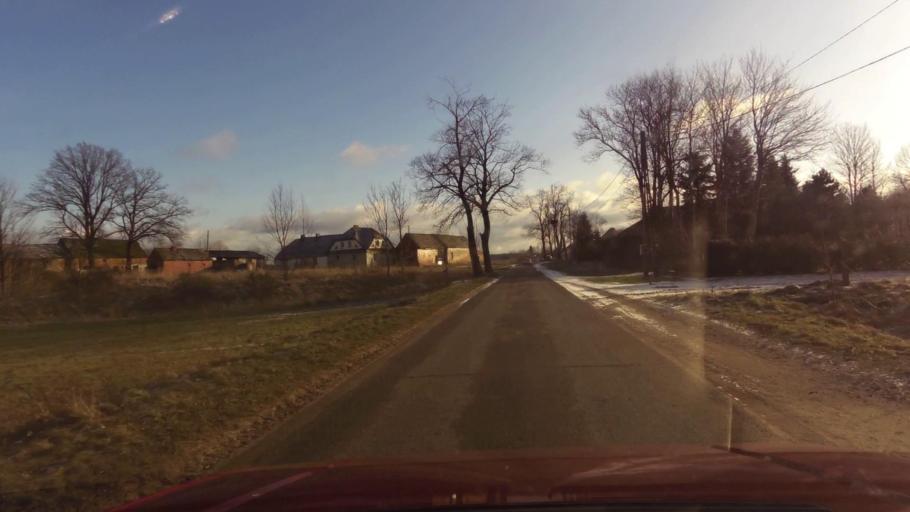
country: PL
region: West Pomeranian Voivodeship
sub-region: Powiat bialogardzki
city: Bialogard
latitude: 54.0799
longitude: 16.0887
